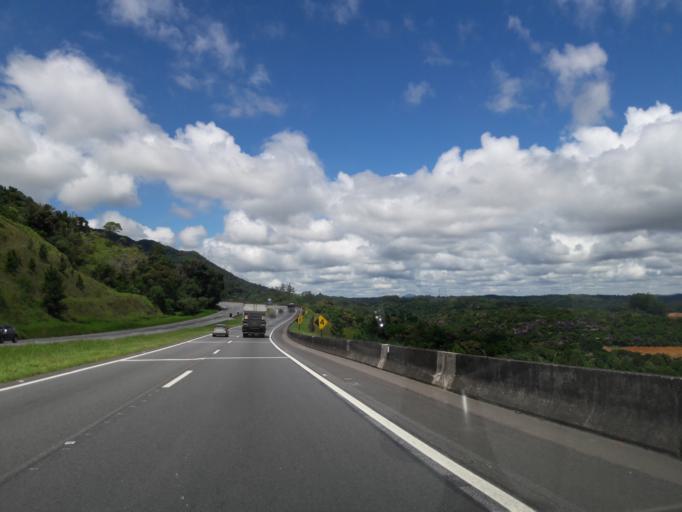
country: BR
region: Parana
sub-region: Campina Grande Do Sul
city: Campina Grande do Sul
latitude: -25.1575
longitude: -48.8616
